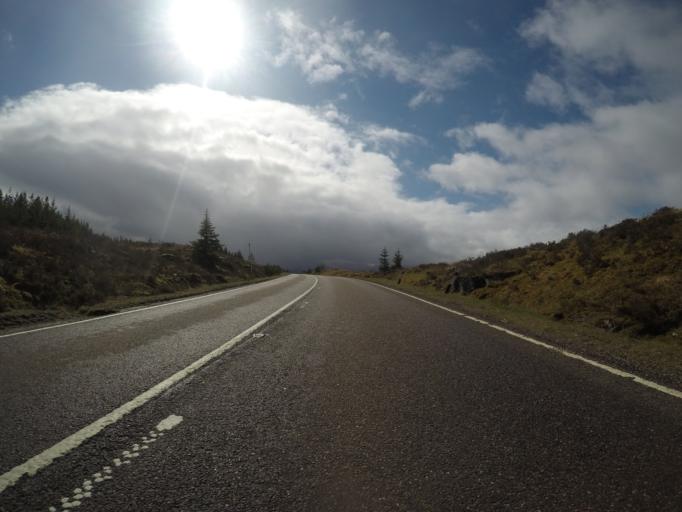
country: GB
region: Scotland
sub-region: Highland
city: Spean Bridge
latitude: 57.0959
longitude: -4.9948
